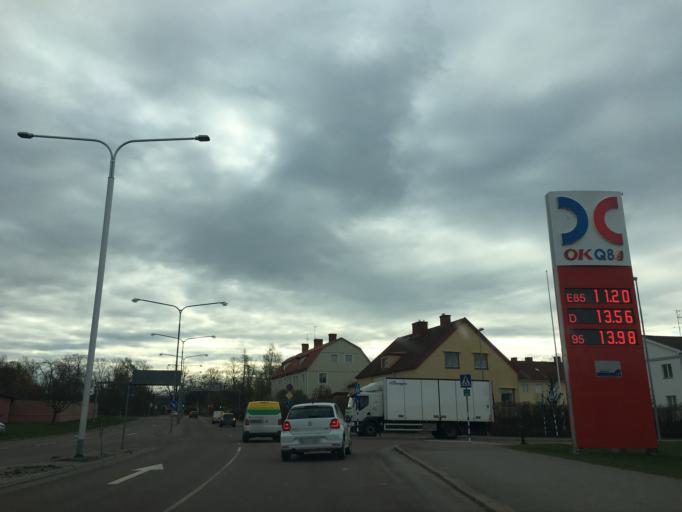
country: SE
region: Vaermland
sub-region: Kristinehamns Kommun
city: Kristinehamn
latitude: 59.3150
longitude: 14.1034
